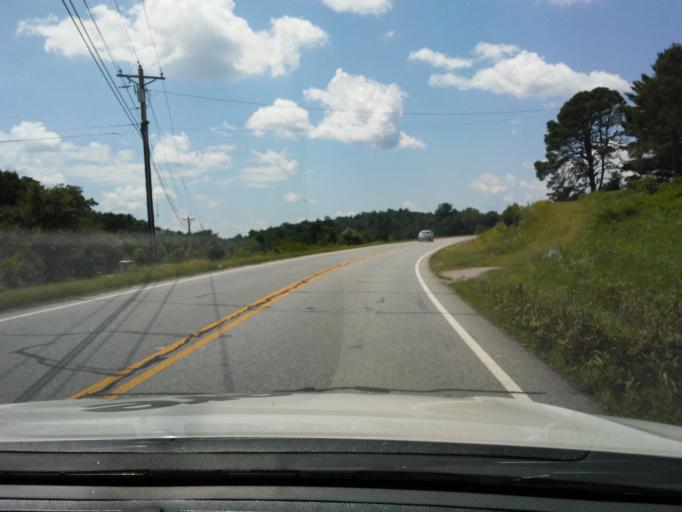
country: US
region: Georgia
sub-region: Towns County
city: Hiawassee
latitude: 34.9768
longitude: -83.7513
